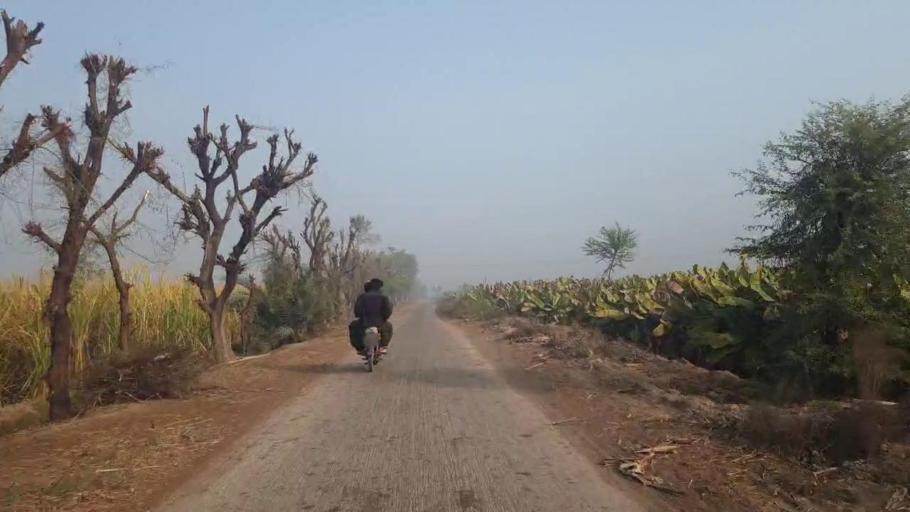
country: PK
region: Sindh
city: Tando Adam
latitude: 25.7865
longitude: 68.6334
